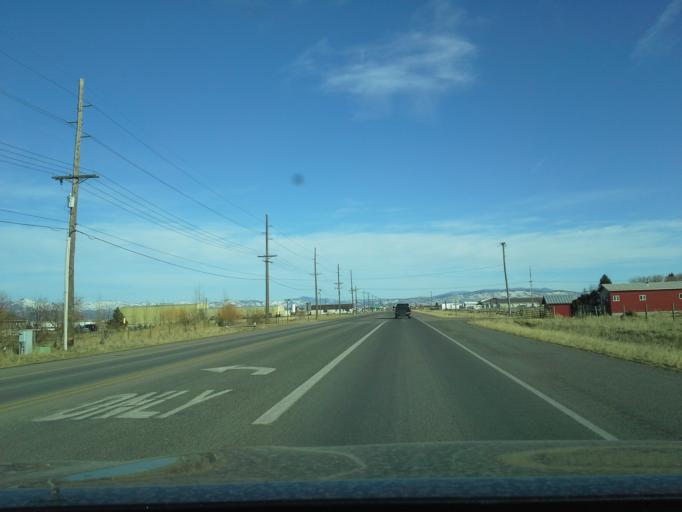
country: US
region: Montana
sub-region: Lewis and Clark County
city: Helena Valley Southeast
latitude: 46.6168
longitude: -111.9454
